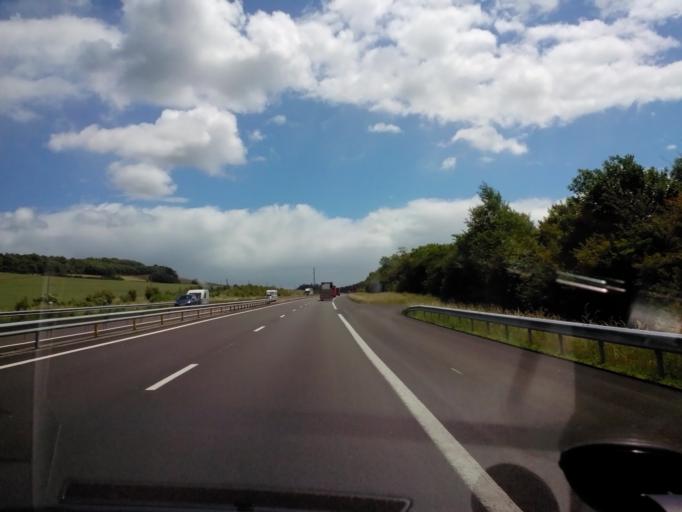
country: FR
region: Champagne-Ardenne
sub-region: Departement de la Haute-Marne
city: Nogent-le-Bas
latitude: 47.9564
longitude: 5.4127
